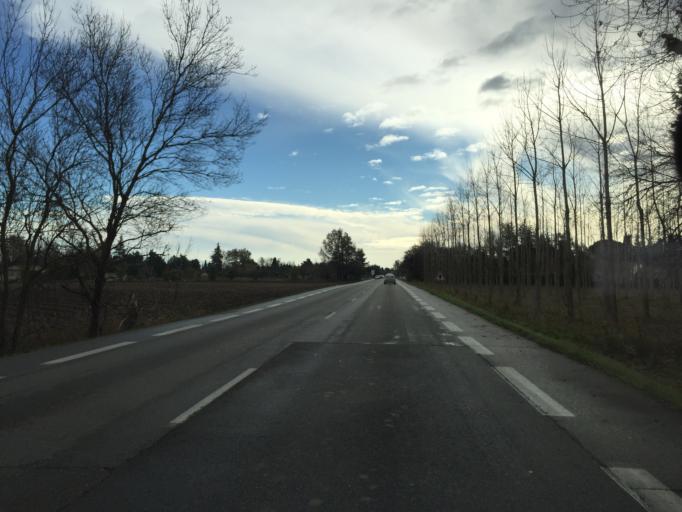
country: FR
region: Provence-Alpes-Cote d'Azur
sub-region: Departement du Vaucluse
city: Velleron
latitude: 43.9381
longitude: 5.0294
